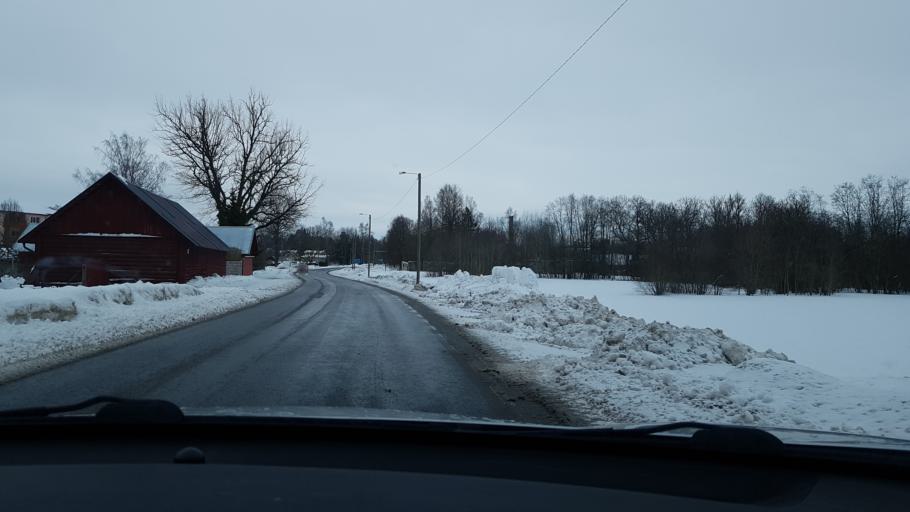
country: EE
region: Jaervamaa
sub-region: Jaerva-Jaani vald
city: Jarva-Jaani
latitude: 59.1473
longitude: 25.7522
